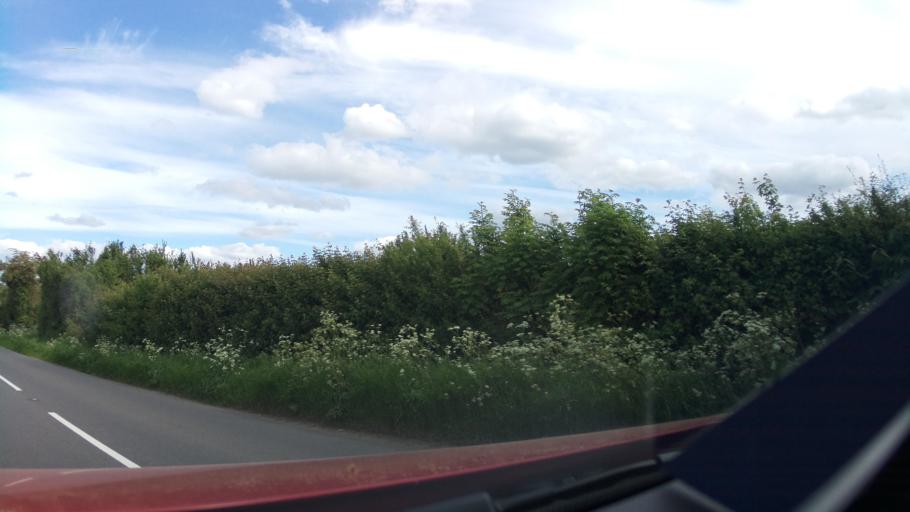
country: GB
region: England
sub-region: Worcestershire
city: Broadway
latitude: 52.0717
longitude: -1.8270
